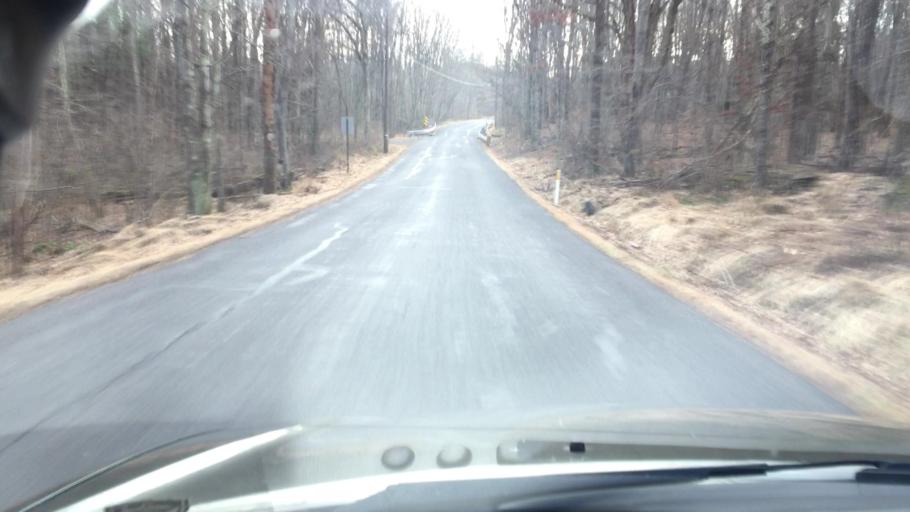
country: US
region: Pennsylvania
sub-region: Luzerne County
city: Back Mountain
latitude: 41.2954
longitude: -76.0474
